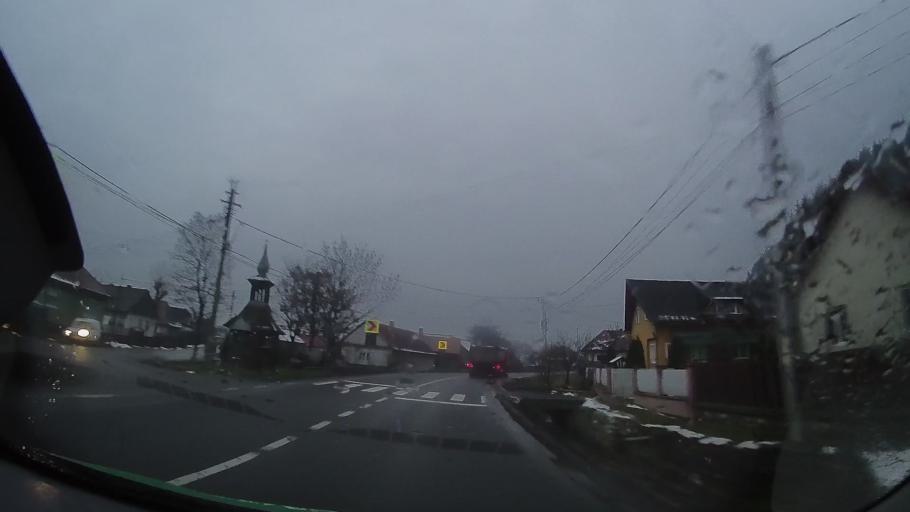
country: RO
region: Harghita
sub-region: Comuna Lazarea
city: Lazarea
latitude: 46.7499
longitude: 25.5208
